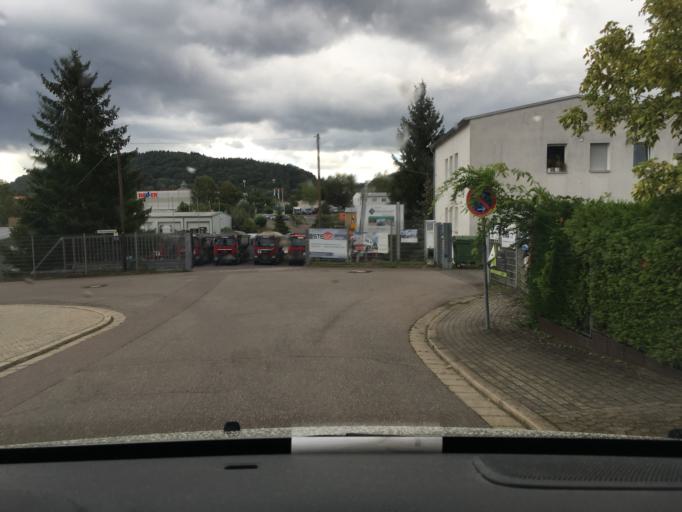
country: DE
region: Saarland
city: Sankt Ingbert
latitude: 49.2724
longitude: 7.1248
